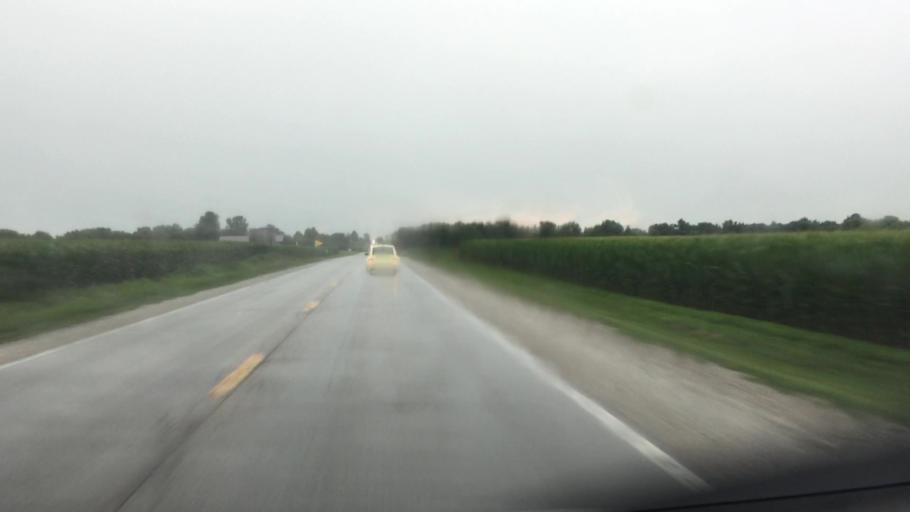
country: US
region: Illinois
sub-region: Hancock County
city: Carthage
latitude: 40.4526
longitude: -91.1397
